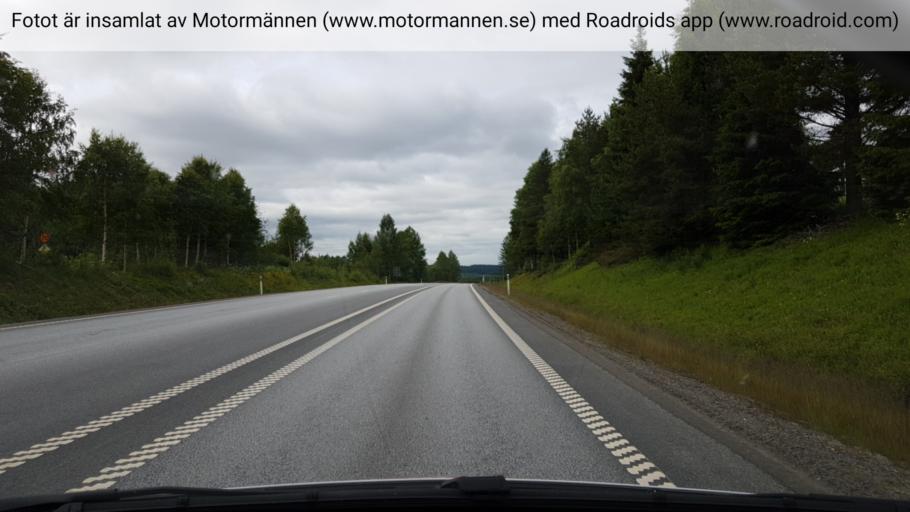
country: SE
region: Vaesterbotten
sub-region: Vannas Kommun
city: Vannasby
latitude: 63.9210
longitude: 19.7999
